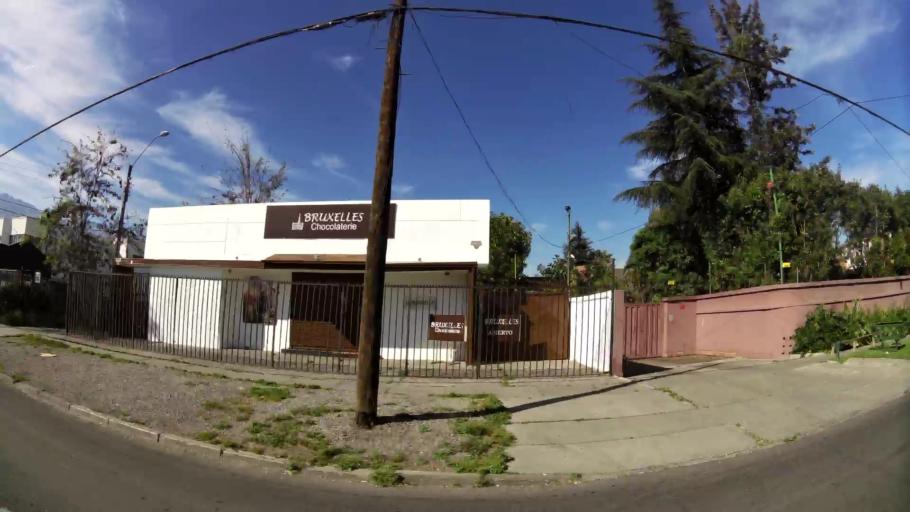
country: CL
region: Santiago Metropolitan
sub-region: Provincia de Santiago
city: Villa Presidente Frei, Nunoa, Santiago, Chile
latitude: -33.4385
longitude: -70.5638
